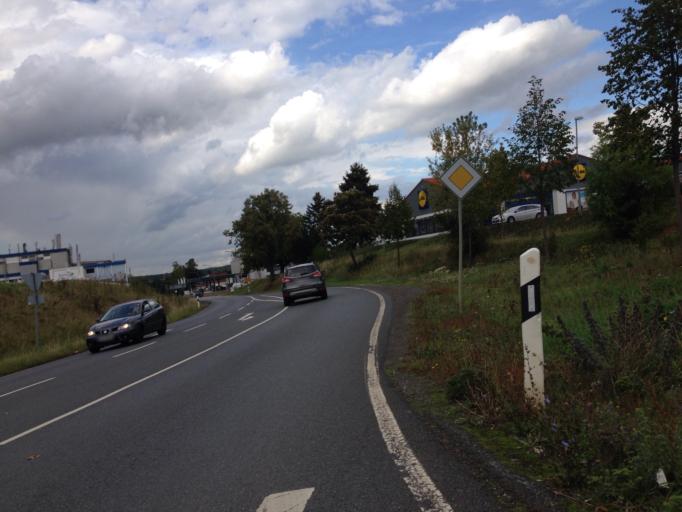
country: DE
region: Hesse
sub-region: Regierungsbezirk Giessen
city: Hungen
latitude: 50.4697
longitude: 8.9103
